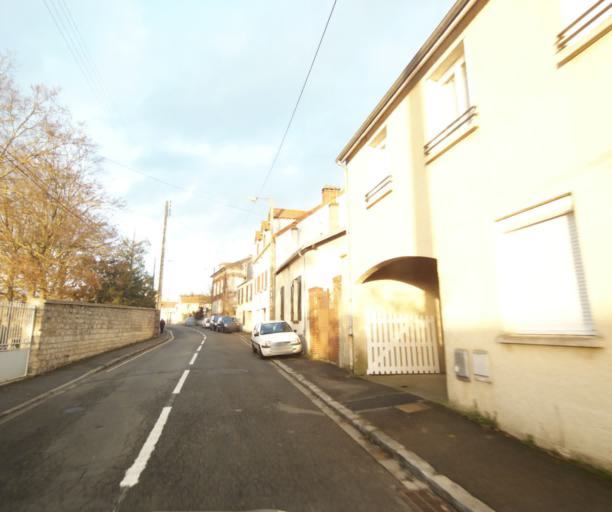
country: FR
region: Ile-de-France
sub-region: Departement des Yvelines
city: Meulan-en-Yvelines
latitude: 49.0069
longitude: 1.9082
